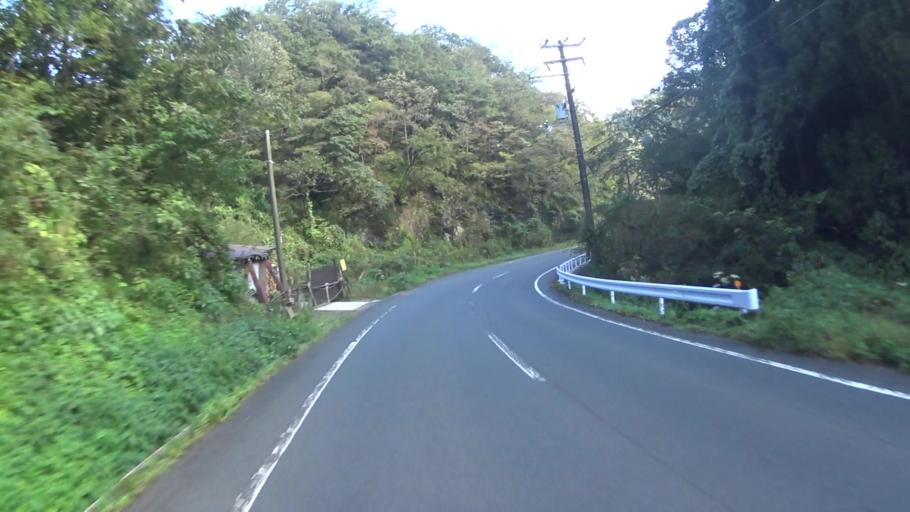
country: JP
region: Kyoto
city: Miyazu
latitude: 35.6343
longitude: 135.1241
